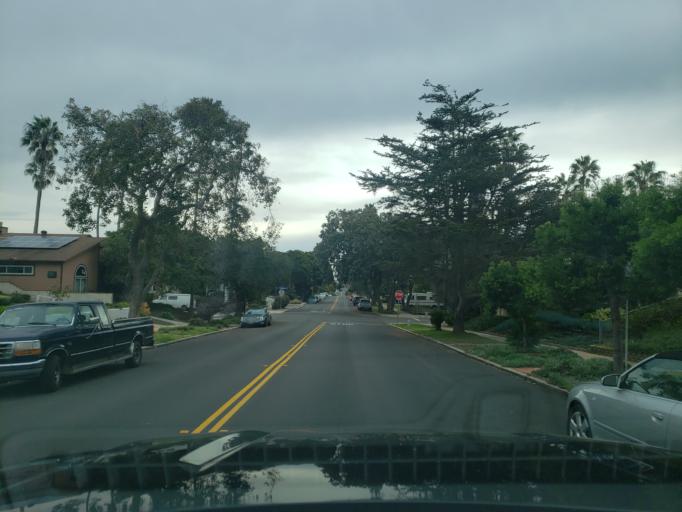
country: US
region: California
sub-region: San Diego County
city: Coronado
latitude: 32.7366
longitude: -117.2448
